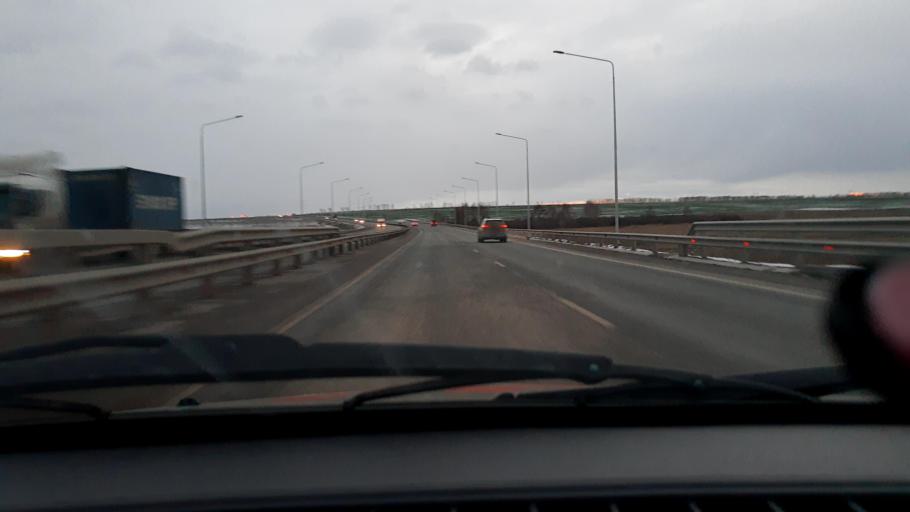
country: RU
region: Bashkortostan
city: Tolbazy
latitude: 54.3087
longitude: 55.8823
